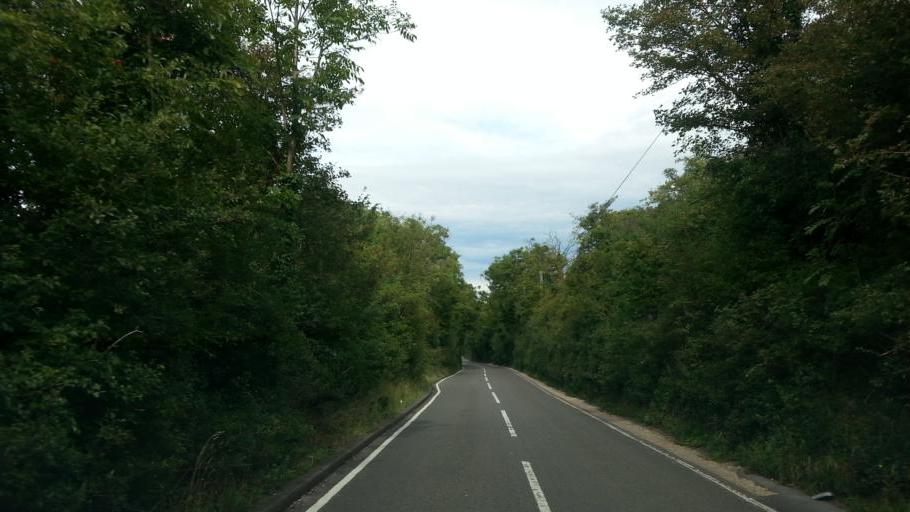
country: GB
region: England
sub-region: Cambridgeshire
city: Fulbourn
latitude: 52.1802
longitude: 0.1686
